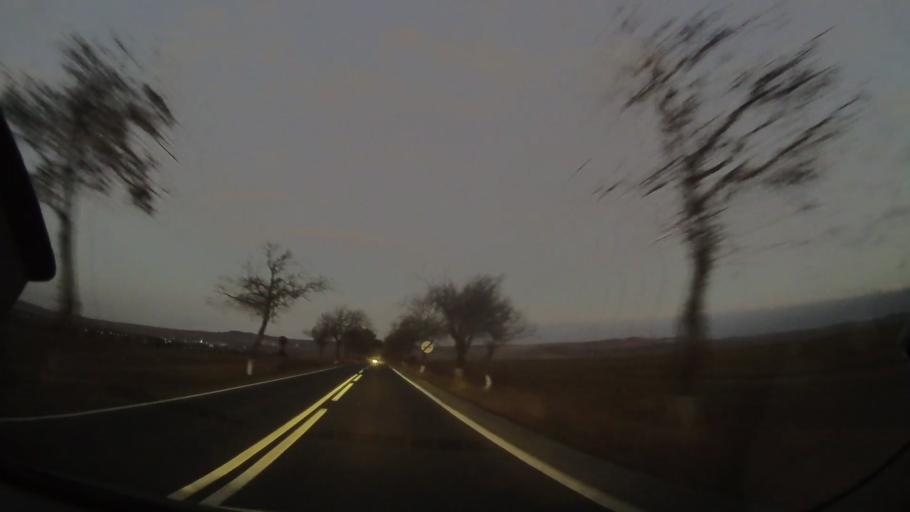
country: RO
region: Tulcea
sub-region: Comuna Frecatei
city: Cataloi
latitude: 45.0841
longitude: 28.7052
